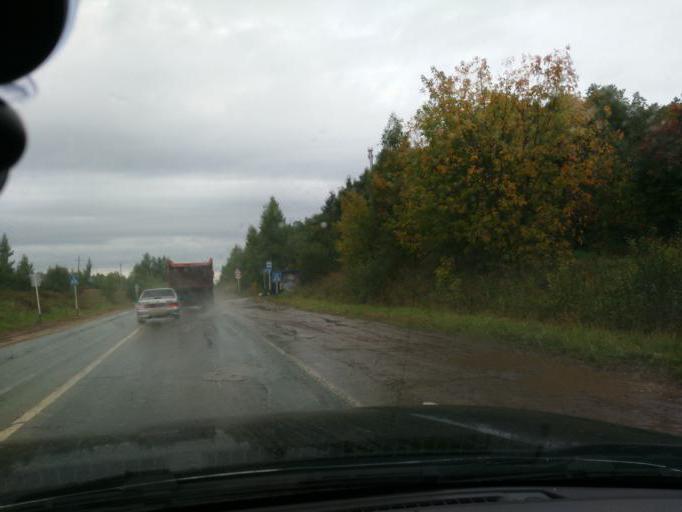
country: RU
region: Perm
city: Kultayevo
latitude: 57.8392
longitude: 55.8235
